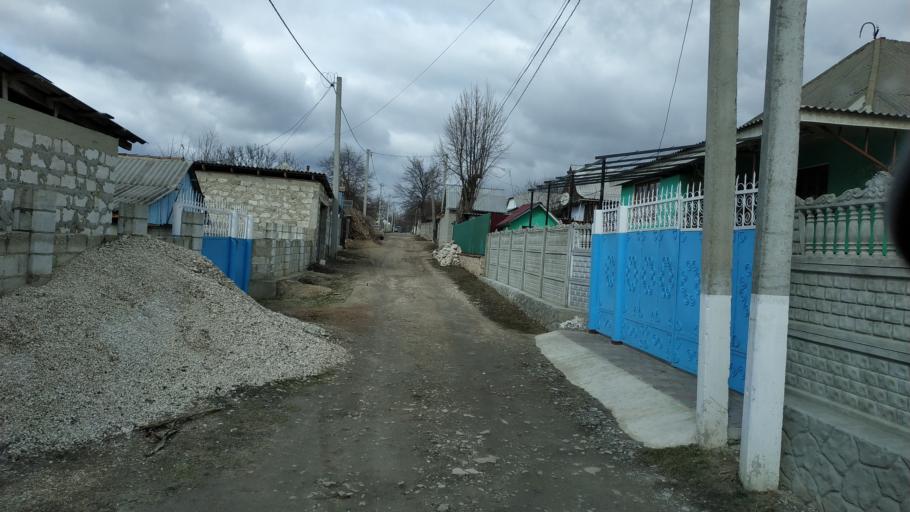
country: MD
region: Stinga Nistrului
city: Bucovat
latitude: 47.2226
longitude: 28.4415
